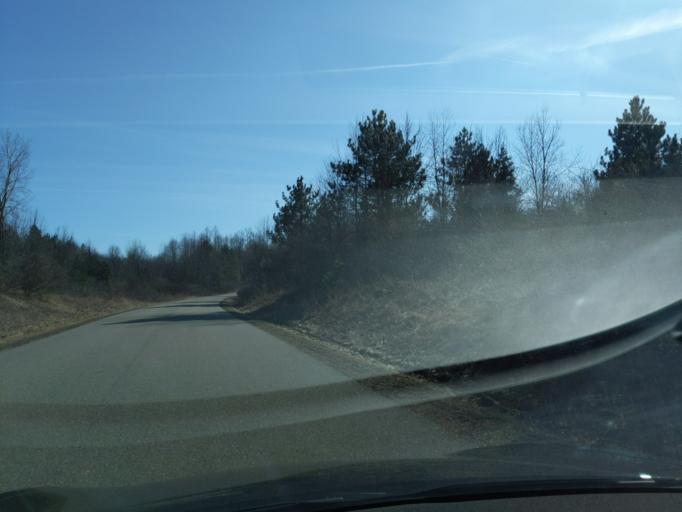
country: US
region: Michigan
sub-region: Ionia County
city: Ionia
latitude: 42.9427
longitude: -85.1352
